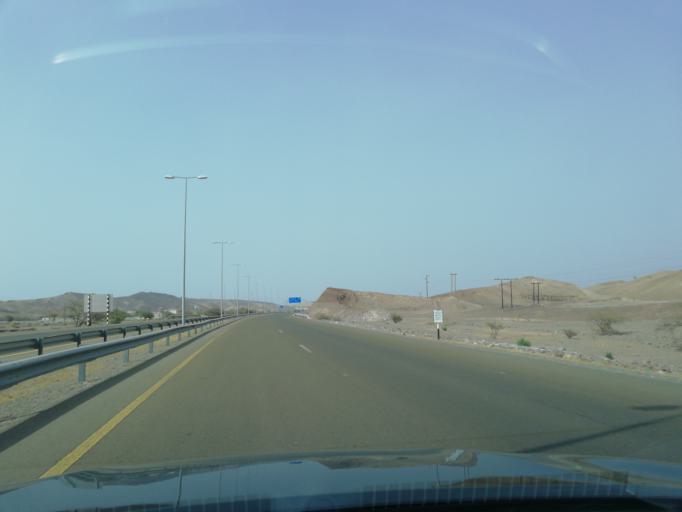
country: OM
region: Al Batinah
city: Al Liwa'
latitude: 24.3673
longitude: 56.5330
